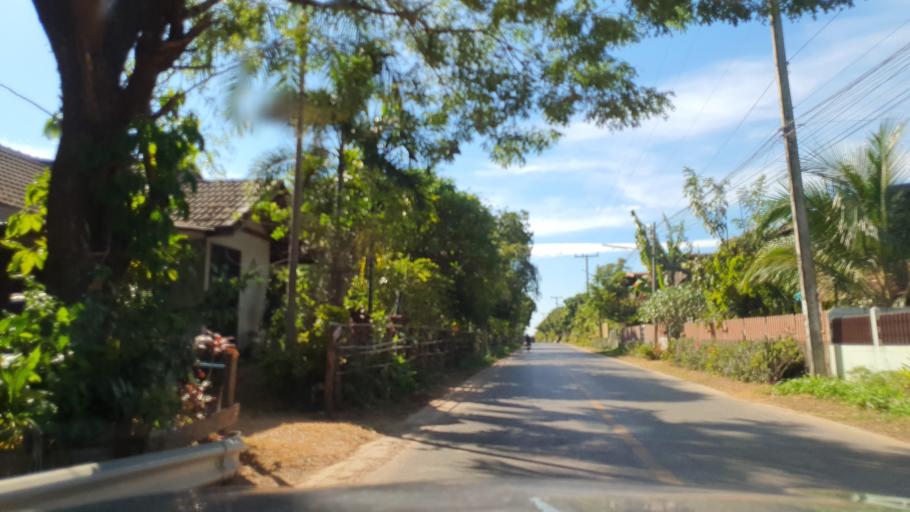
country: TH
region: Kalasin
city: Khao Wong
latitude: 16.6434
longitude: 104.1404
